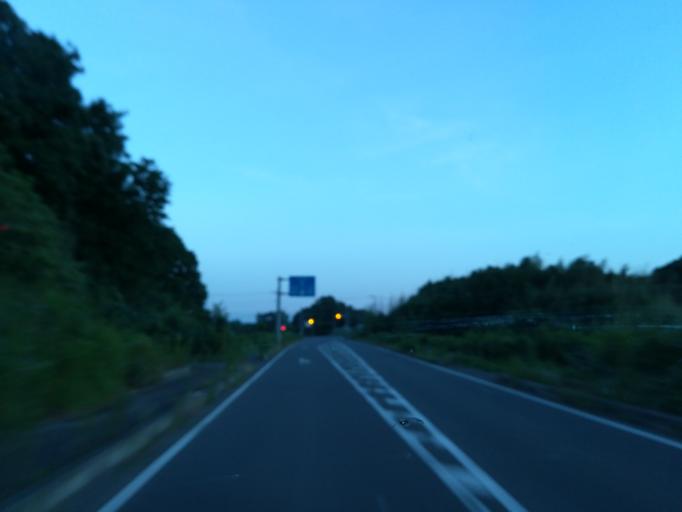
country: JP
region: Ibaraki
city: Makabe
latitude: 36.2656
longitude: 140.0585
